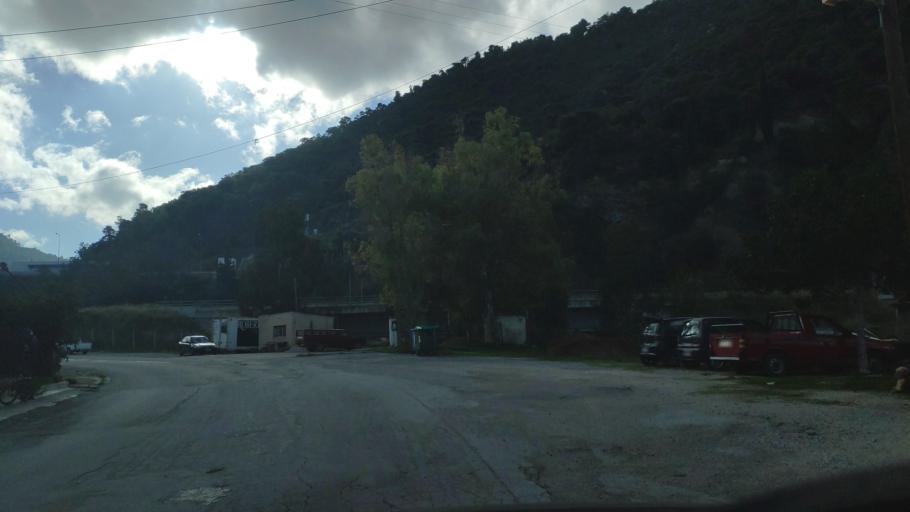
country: GR
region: West Greece
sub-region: Nomos Achaias
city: Aiyira
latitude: 38.1321
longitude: 22.4279
